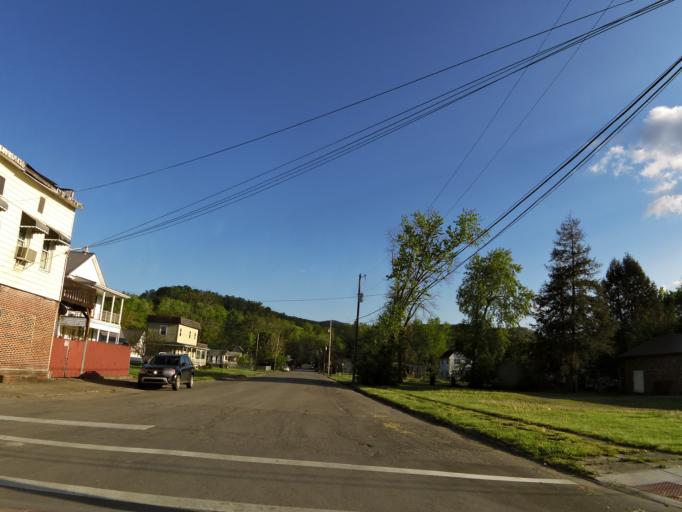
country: US
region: Kentucky
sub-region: Bell County
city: Middlesboro
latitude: 36.6048
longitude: -83.7155
